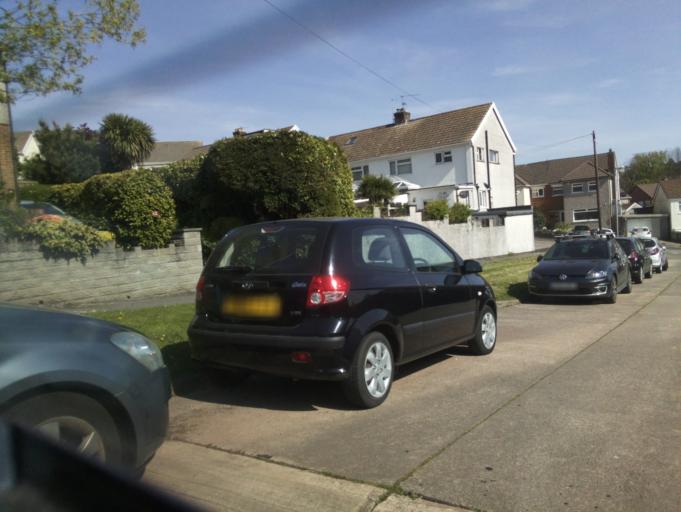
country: GB
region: Wales
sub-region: Cardiff
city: Radyr
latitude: 51.5282
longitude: -3.2318
